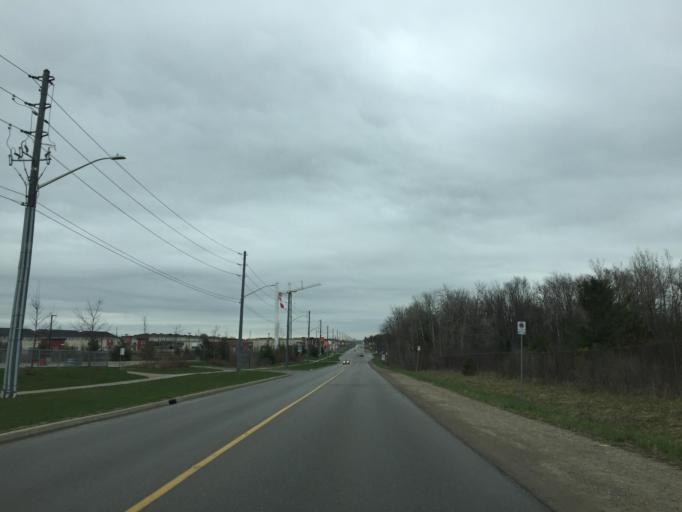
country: CA
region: Ontario
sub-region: Wellington County
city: Guelph
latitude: 43.5801
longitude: -80.2272
